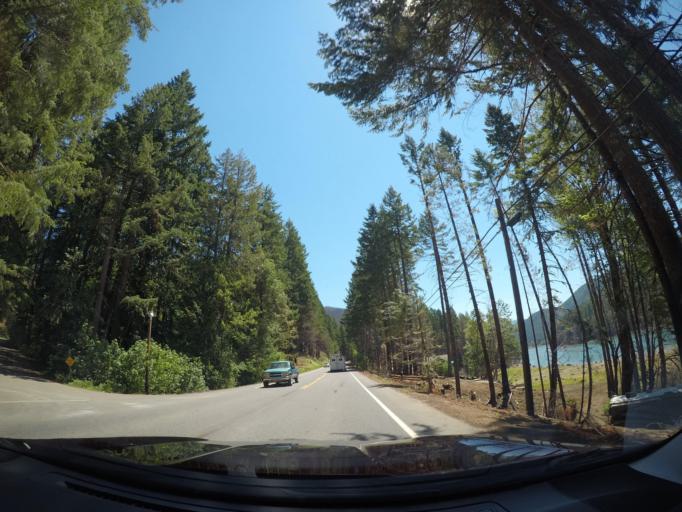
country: US
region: Oregon
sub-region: Linn County
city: Mill City
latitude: 44.7288
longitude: -122.1420
